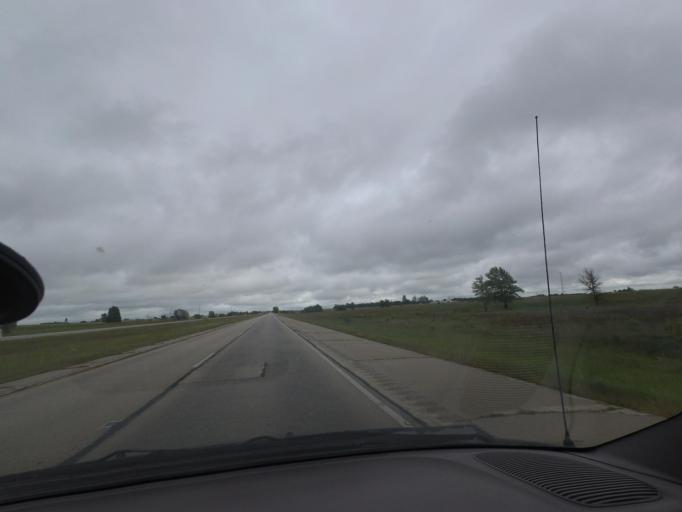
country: US
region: Illinois
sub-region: Piatt County
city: Cerro Gordo
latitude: 40.0164
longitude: -88.7448
